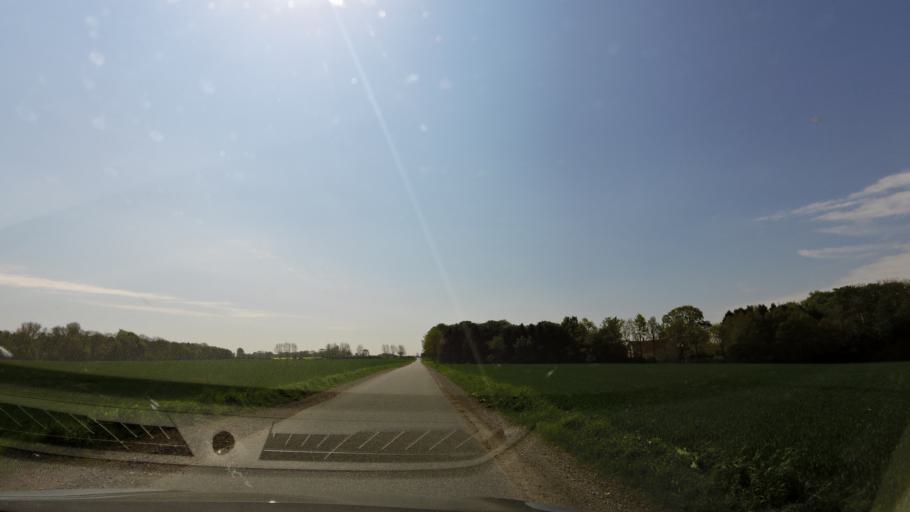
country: DK
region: South Denmark
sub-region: Nyborg Kommune
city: Ullerslev
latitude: 55.2707
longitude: 10.6901
